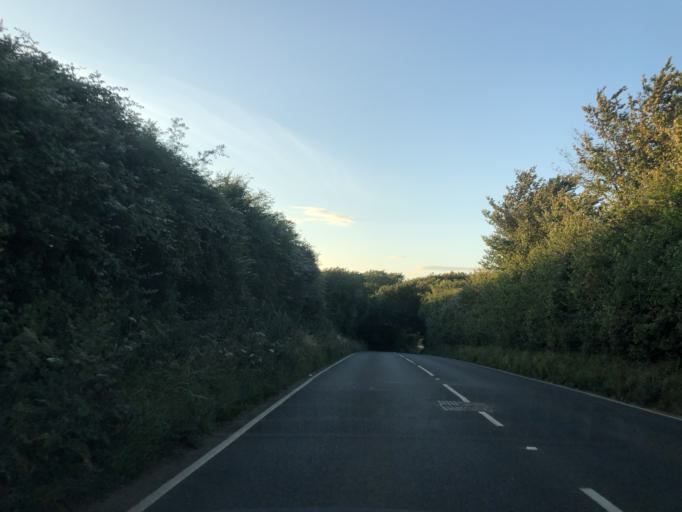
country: GB
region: England
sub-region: Isle of Wight
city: Newport
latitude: 50.6635
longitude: -1.2847
